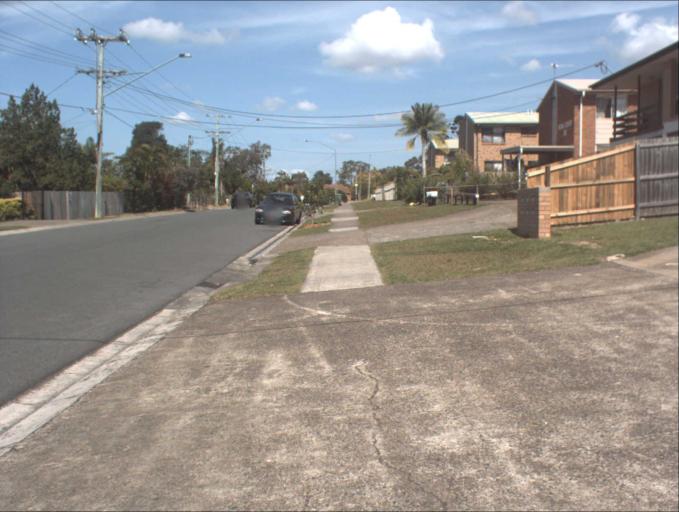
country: AU
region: Queensland
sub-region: Logan
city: Woodridge
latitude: -27.6353
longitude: 153.1037
